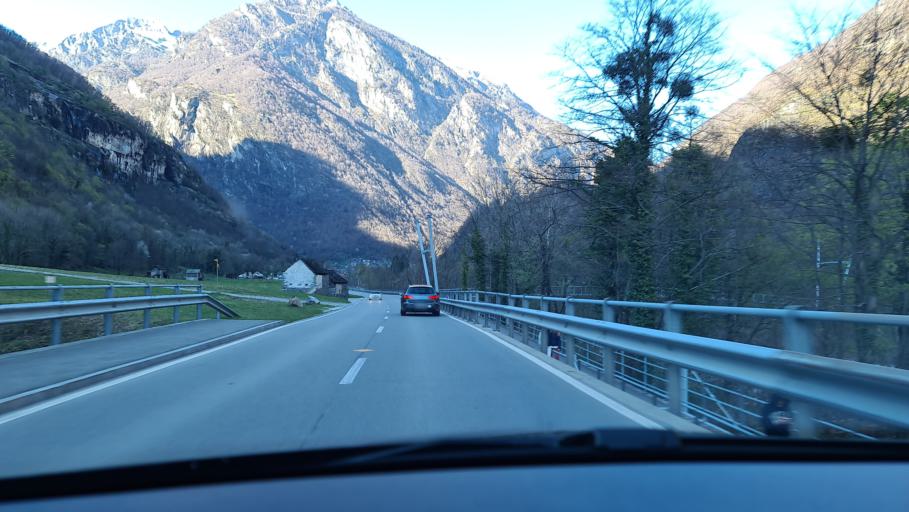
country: CH
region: Ticino
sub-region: Vallemaggia District
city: Cevio
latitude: 46.3285
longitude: 8.6065
